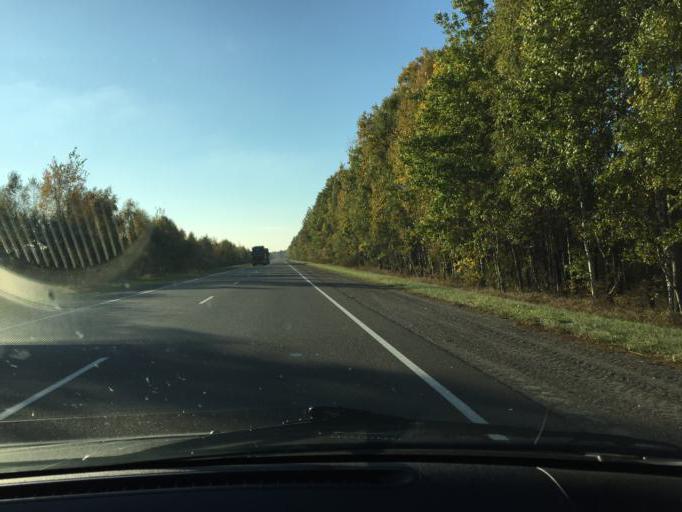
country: BY
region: Brest
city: Horad Luninyets
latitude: 52.3176
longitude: 26.6070
